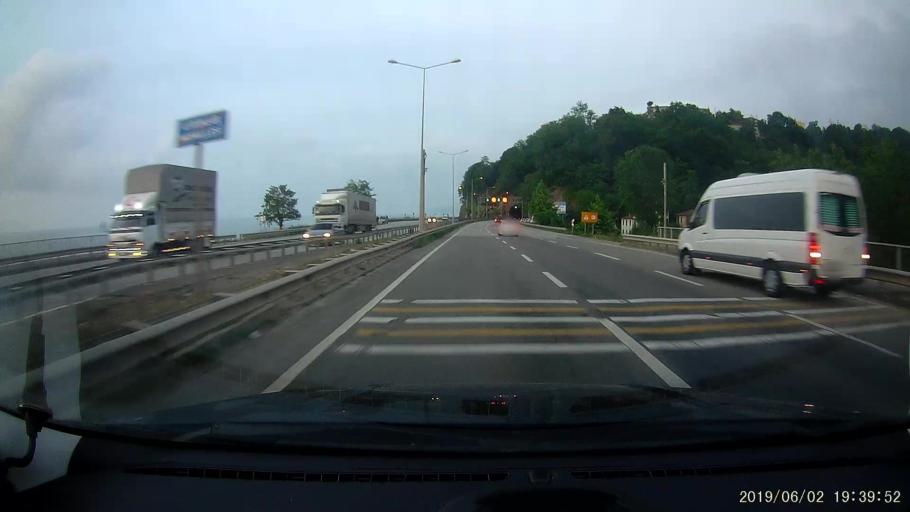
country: TR
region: Giresun
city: Kesap
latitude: 40.9149
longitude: 38.4486
